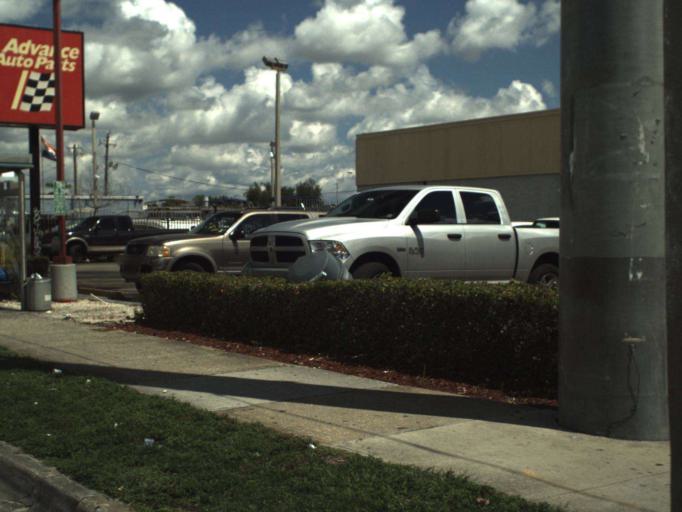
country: US
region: Florida
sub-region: Miami-Dade County
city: Pinewood
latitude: 25.8625
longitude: -80.2096
